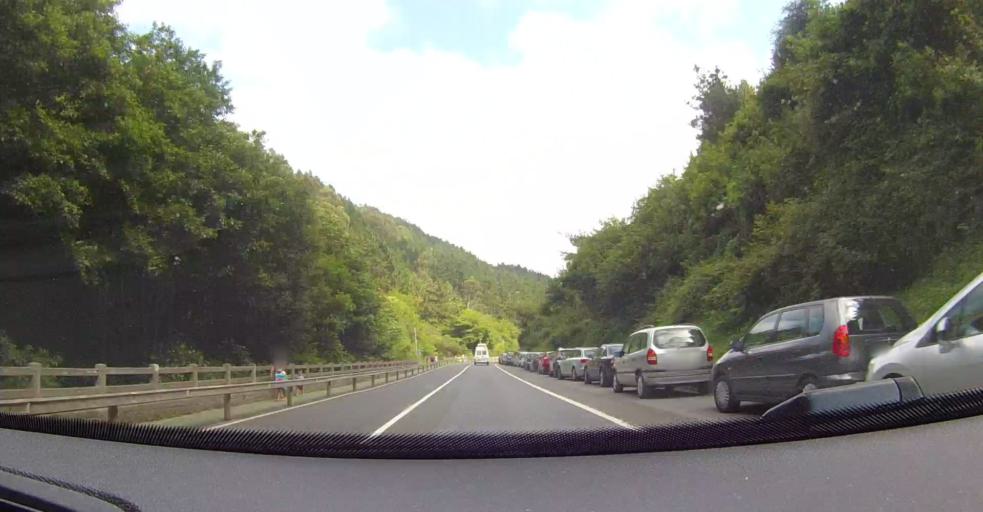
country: ES
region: Basque Country
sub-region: Bizkaia
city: Elantxobe
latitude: 43.4047
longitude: -2.6525
